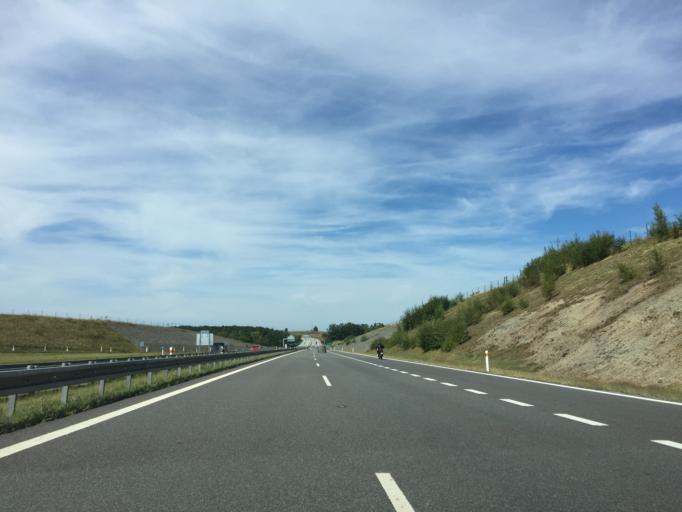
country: CZ
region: Jihocesky
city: Sobeslav
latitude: 49.2678
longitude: 14.7366
